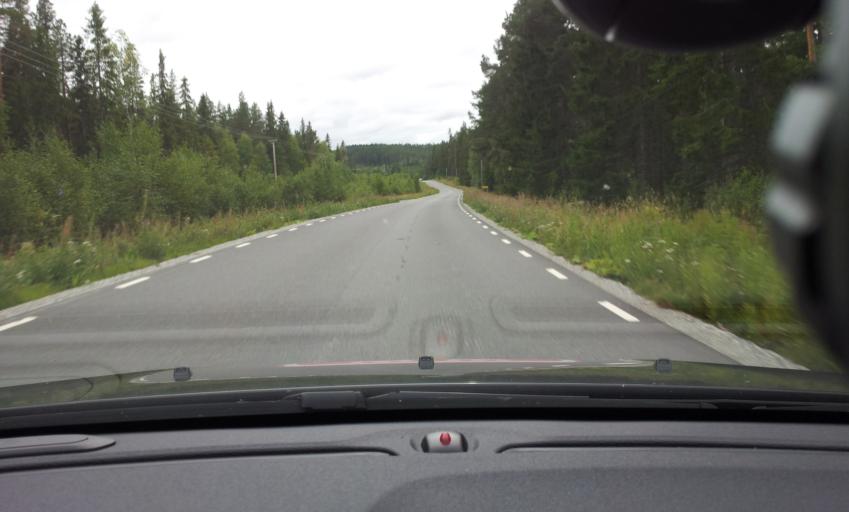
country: SE
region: Jaemtland
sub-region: Braecke Kommun
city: Braecke
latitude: 63.1450
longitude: 15.5401
